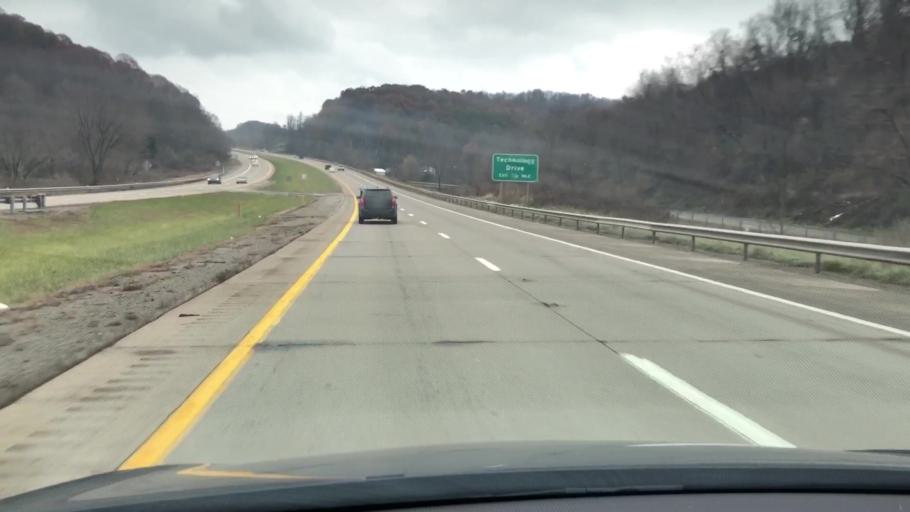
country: US
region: Pennsylvania
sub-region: Westmoreland County
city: New Stanton
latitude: 40.2106
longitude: -79.5894
